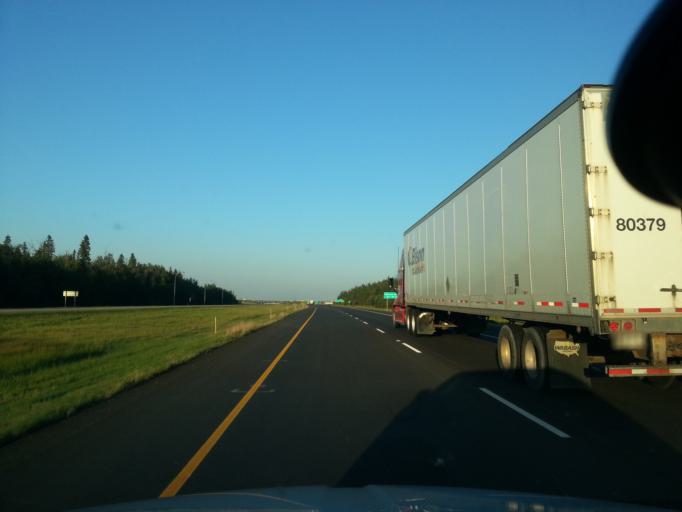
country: CA
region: Alberta
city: Spruce Grove
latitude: 53.5686
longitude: -113.9524
